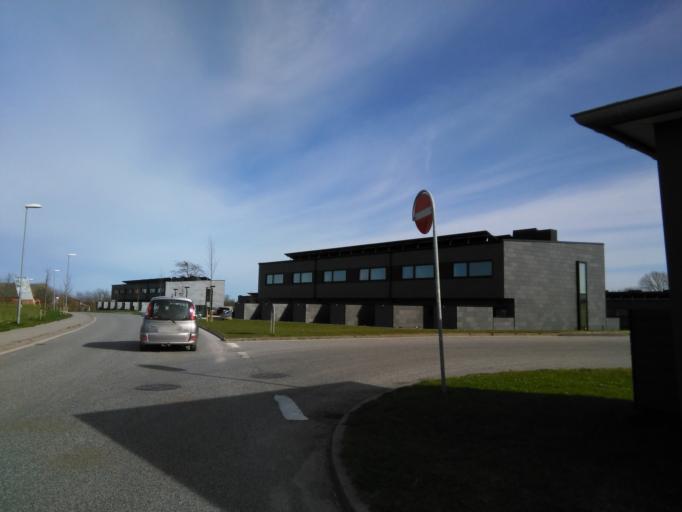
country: DK
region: Central Jutland
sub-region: Arhus Kommune
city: Marslet
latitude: 56.0584
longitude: 10.1648
